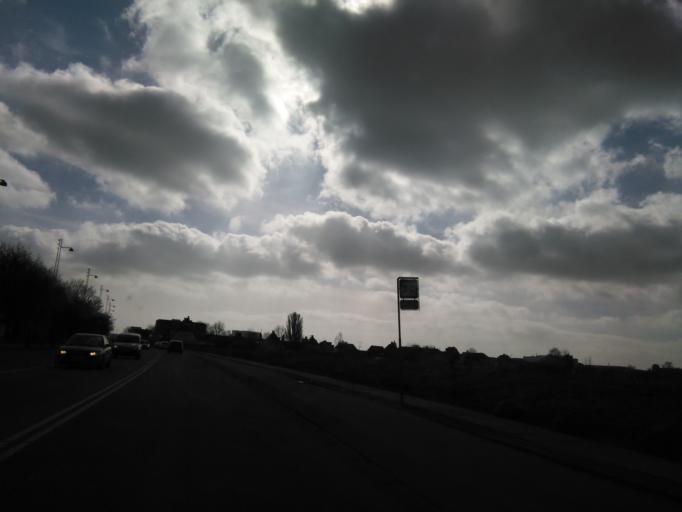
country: DK
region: Capital Region
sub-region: Tarnby Kommune
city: Tarnby
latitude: 55.6426
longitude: 12.6451
